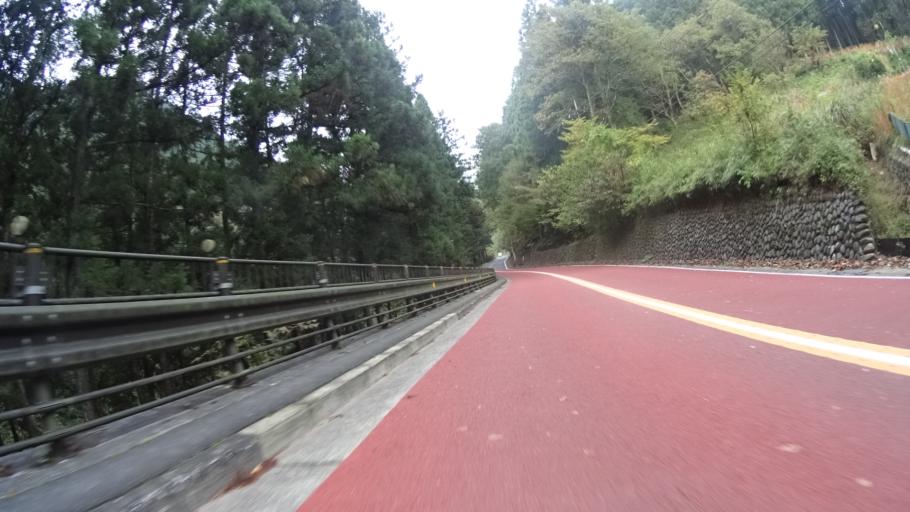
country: JP
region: Tokyo
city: Itsukaichi
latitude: 35.7057
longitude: 139.1529
